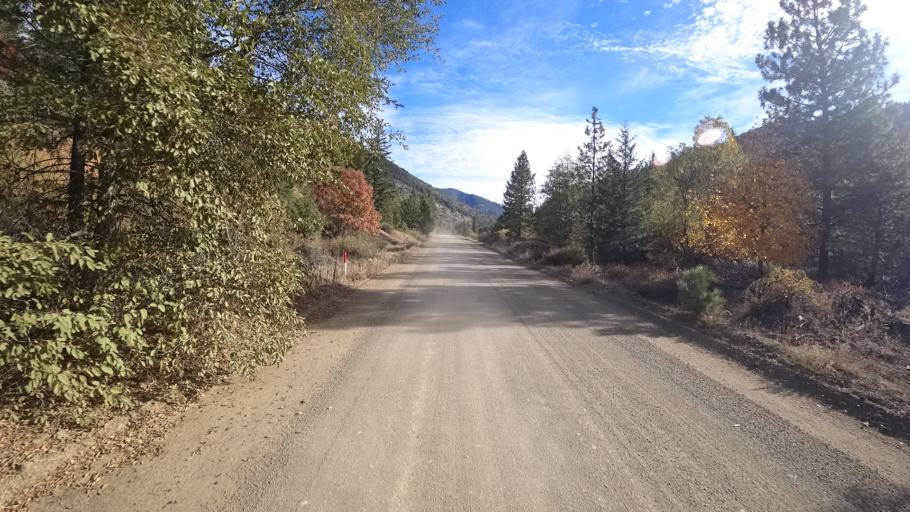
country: US
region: California
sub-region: Siskiyou County
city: Yreka
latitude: 41.7117
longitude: -122.8078
